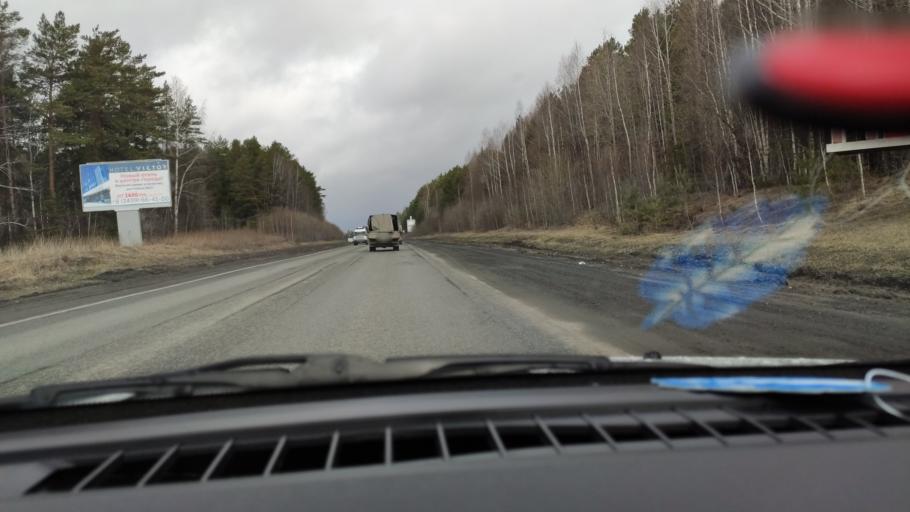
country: RU
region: Sverdlovsk
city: Talitsa
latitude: 56.8724
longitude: 60.0366
